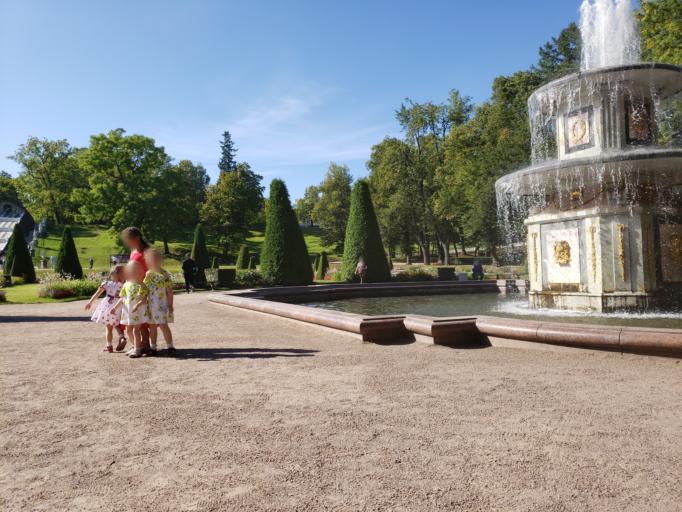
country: RU
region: St.-Petersburg
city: Peterhof
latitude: 59.8842
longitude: 29.9169
